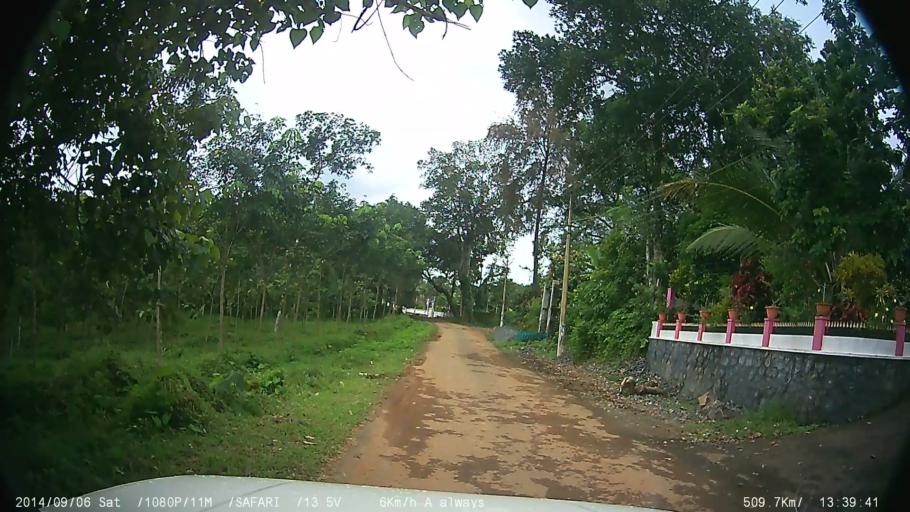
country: IN
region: Kerala
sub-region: Kottayam
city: Palackattumala
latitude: 9.7883
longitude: 76.5635
